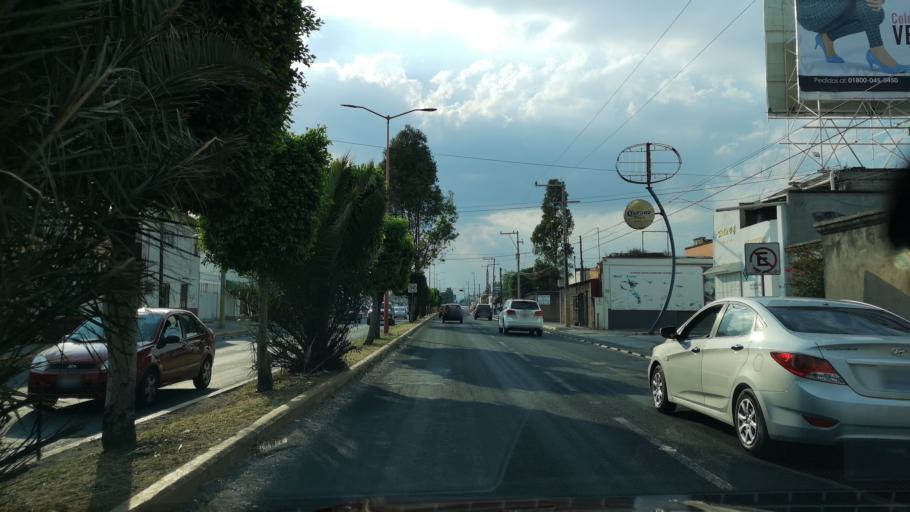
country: MX
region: Puebla
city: Cholula
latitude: 19.0674
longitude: -98.3064
